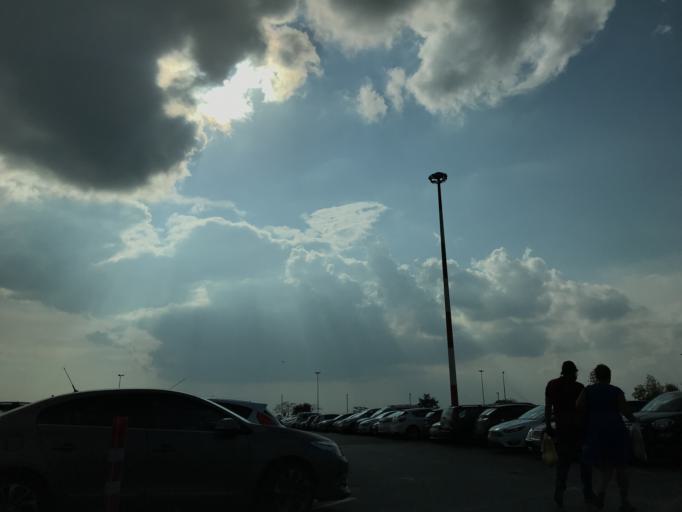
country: TR
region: Istanbul
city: UEskuedar
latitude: 40.9904
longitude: 29.0189
